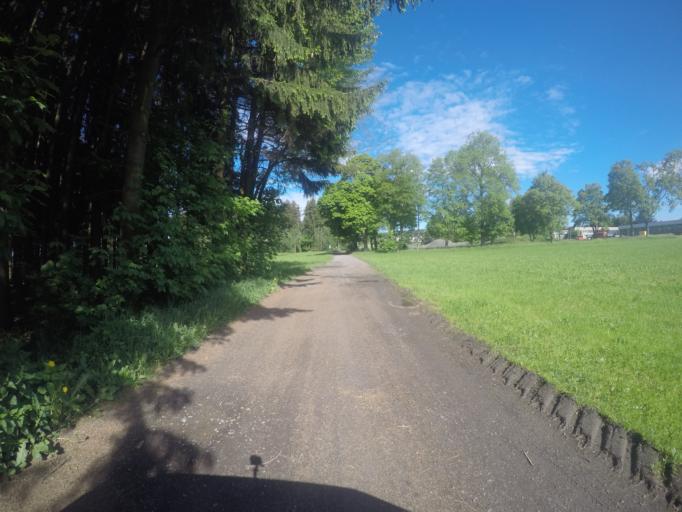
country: DE
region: Bavaria
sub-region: Upper Franconia
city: Schonwald
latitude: 50.1907
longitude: 12.0884
